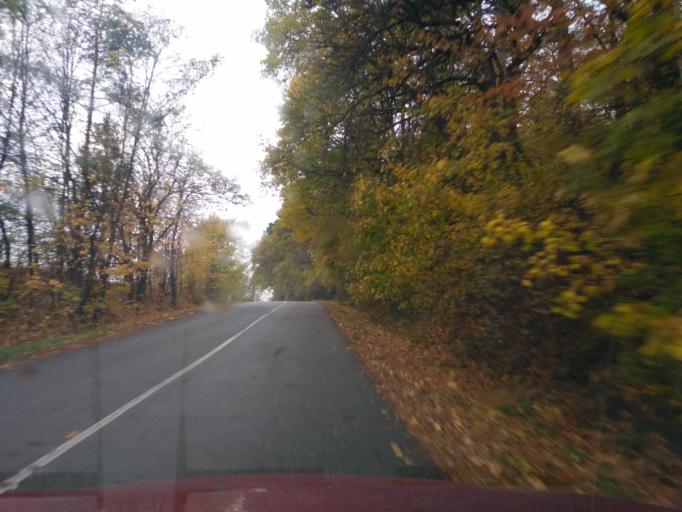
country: SK
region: Kosicky
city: Moldava nad Bodvou
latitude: 48.6735
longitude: 21.1222
